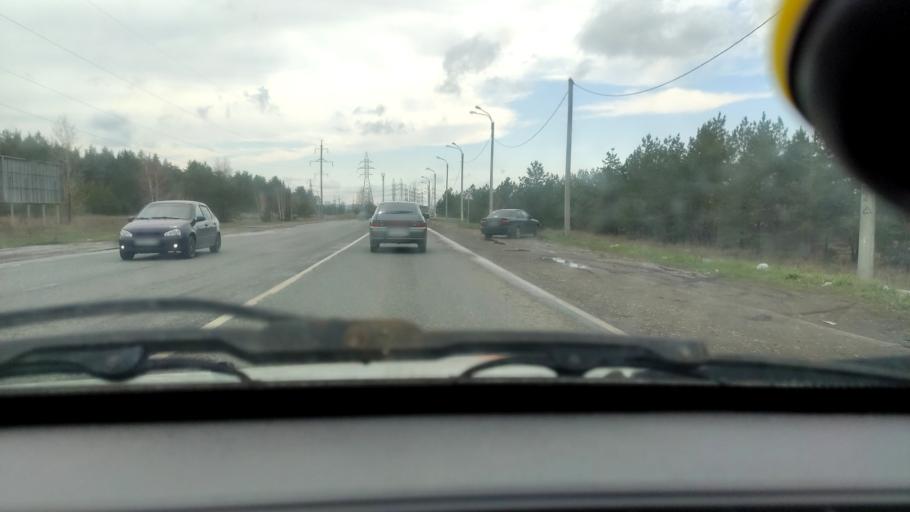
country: RU
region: Samara
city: Zhigulevsk
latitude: 53.5665
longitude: 49.5474
